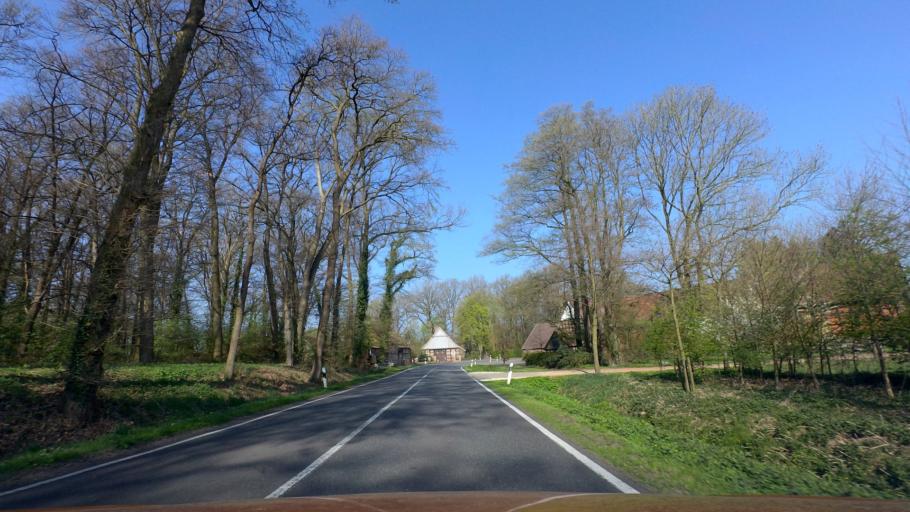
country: DE
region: Lower Saxony
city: Dinklage
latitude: 52.6964
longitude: 8.1589
